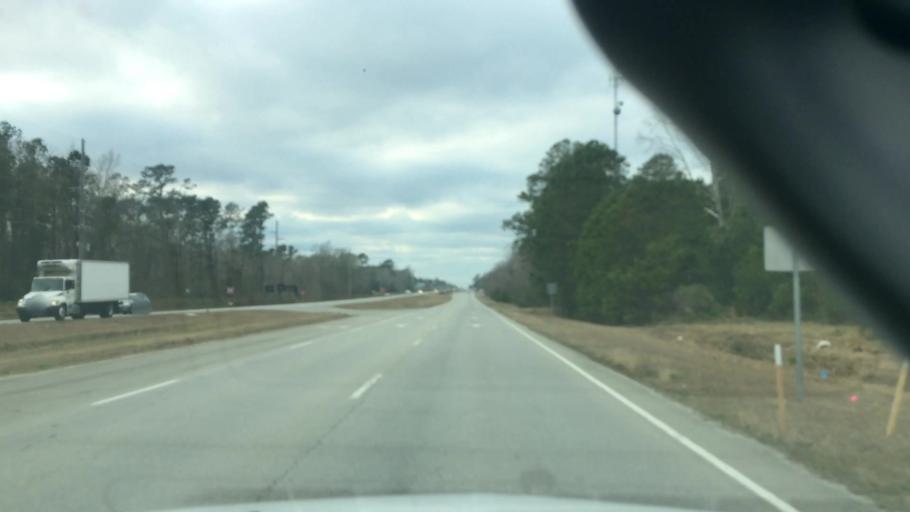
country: US
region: North Carolina
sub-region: Brunswick County
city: Sunset Beach
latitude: 33.9487
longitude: -78.4881
